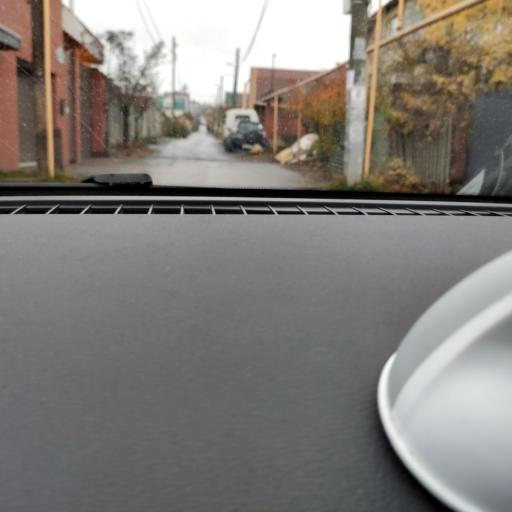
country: RU
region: Samara
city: Samara
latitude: 53.2715
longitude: 50.2105
